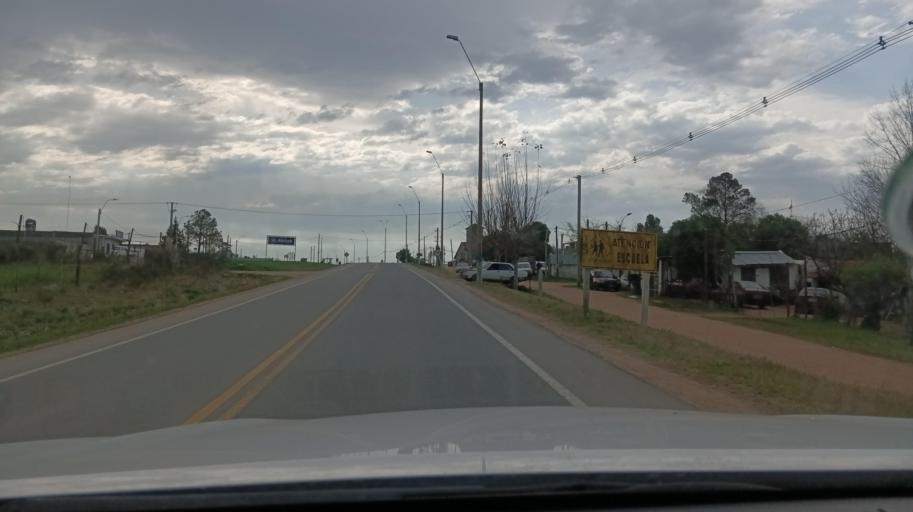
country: UY
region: Canelones
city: Toledo
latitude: -34.7411
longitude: -56.1122
